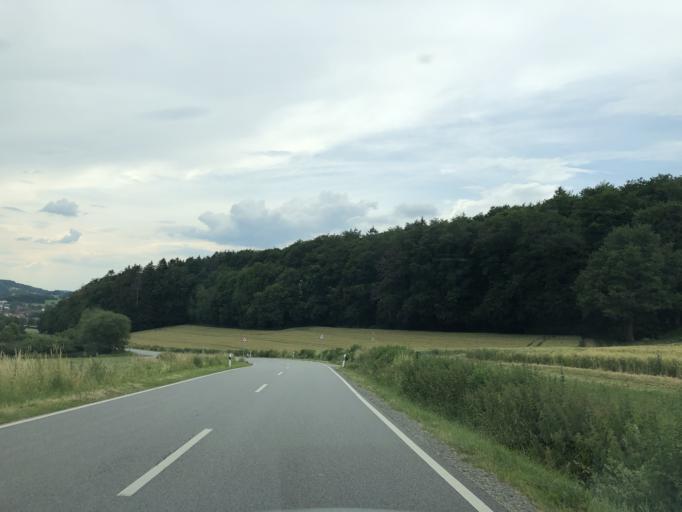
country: DE
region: Hesse
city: Lutzelbach
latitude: 49.7420
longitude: 8.7580
